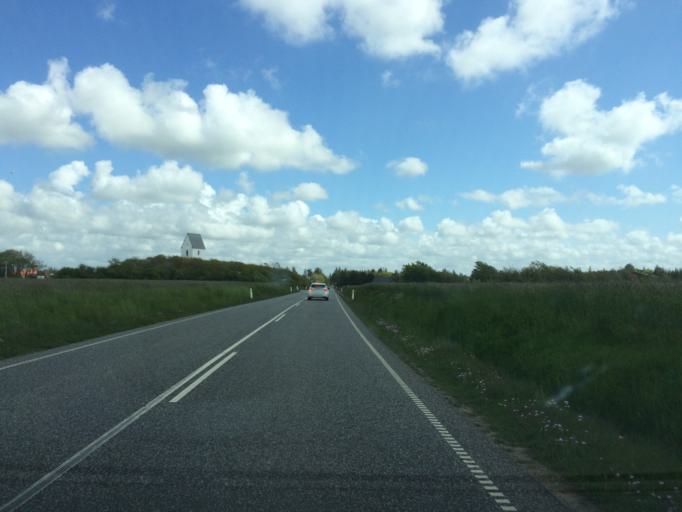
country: DK
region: Central Jutland
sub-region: Holstebro Kommune
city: Ulfborg
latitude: 56.3080
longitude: 8.1812
